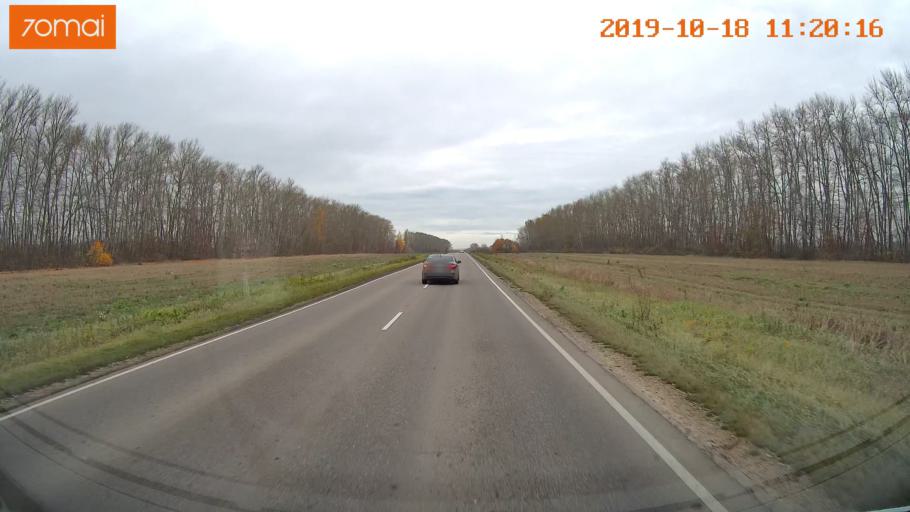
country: RU
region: Tula
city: Kimovsk
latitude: 54.0581
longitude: 38.5578
